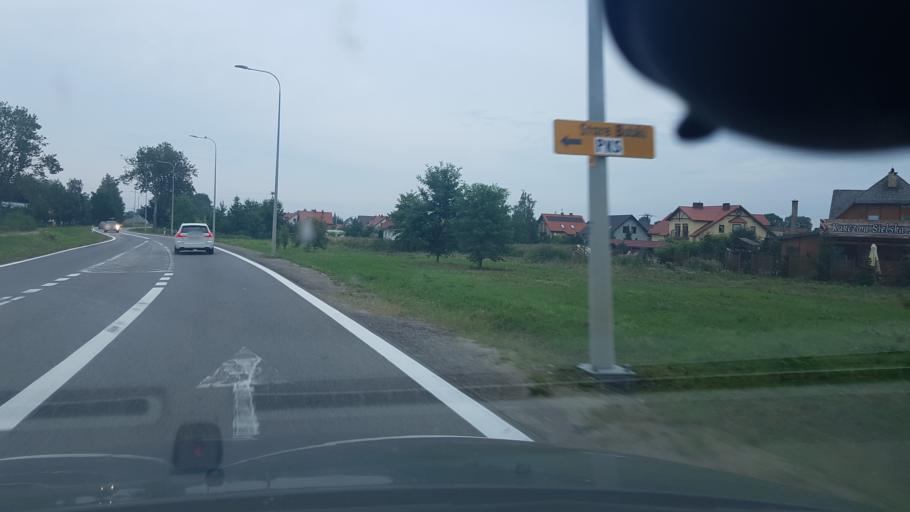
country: PL
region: Pomeranian Voivodeship
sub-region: Powiat nowodworski
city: Nowy Dwor Gdanski
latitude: 54.2146
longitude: 19.1062
